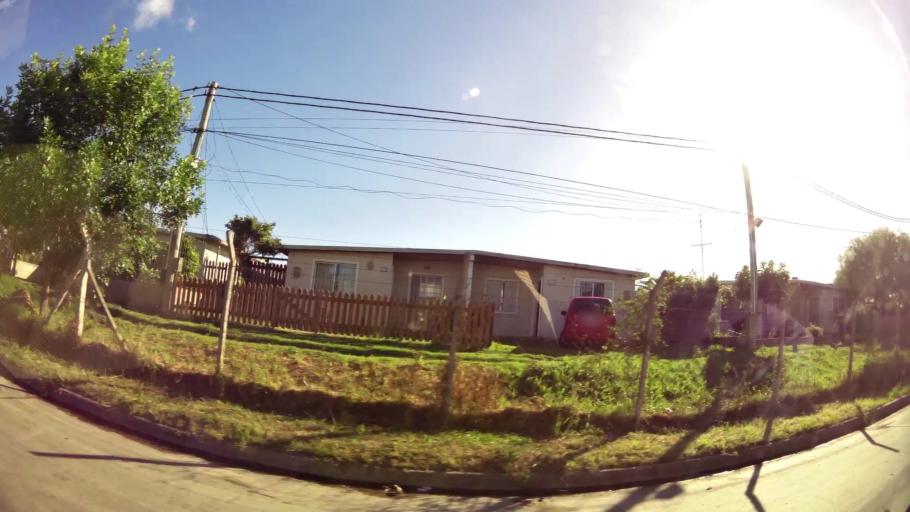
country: UY
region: Montevideo
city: Montevideo
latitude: -34.8411
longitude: -56.2308
